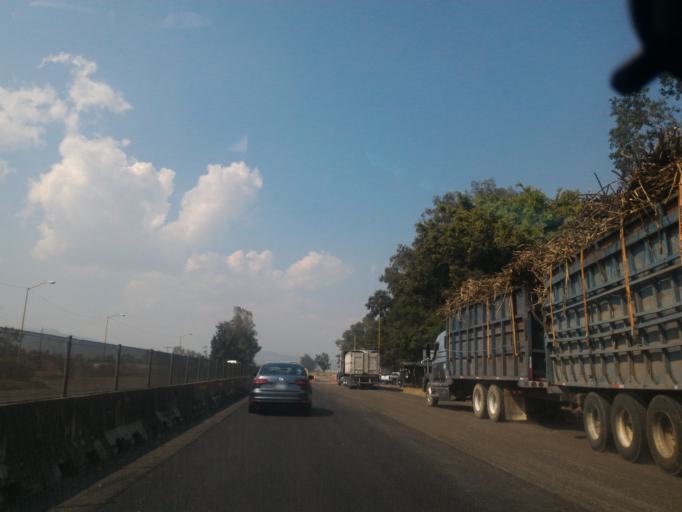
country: MX
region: Jalisco
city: Ciudad Guzman
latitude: 19.7112
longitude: -103.5021
